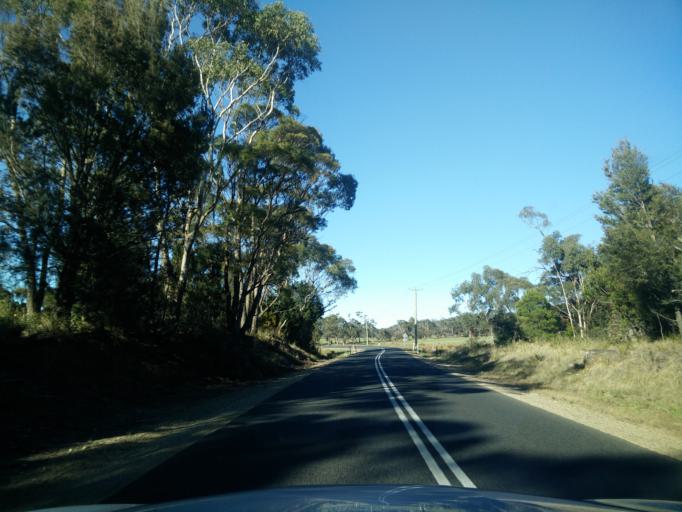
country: AU
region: Tasmania
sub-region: Break O'Day
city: St Helens
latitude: -41.9169
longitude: 148.2468
